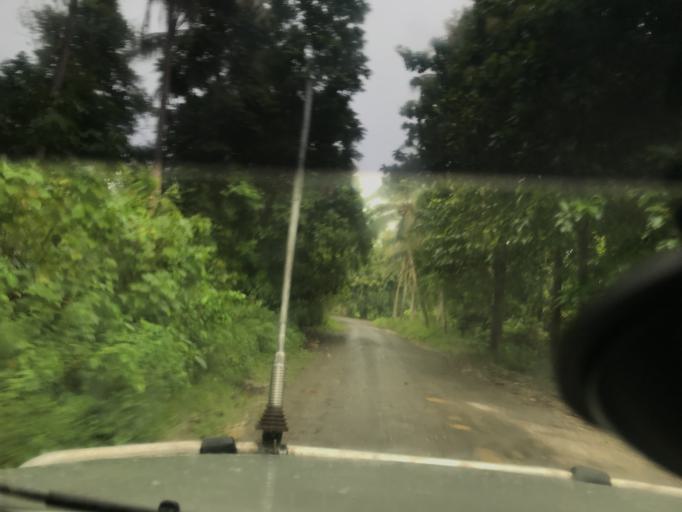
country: SB
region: Malaita
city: Auki
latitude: -8.9709
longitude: 160.7828
